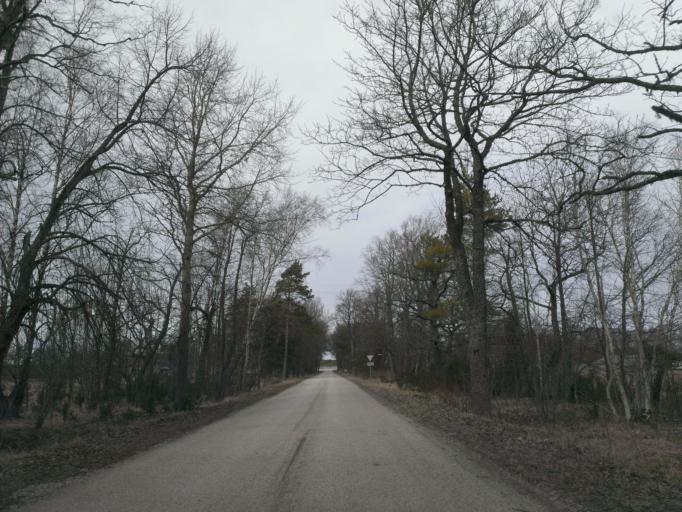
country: EE
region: Laeaene
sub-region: Lihula vald
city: Lihula
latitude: 58.5873
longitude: 23.5373
